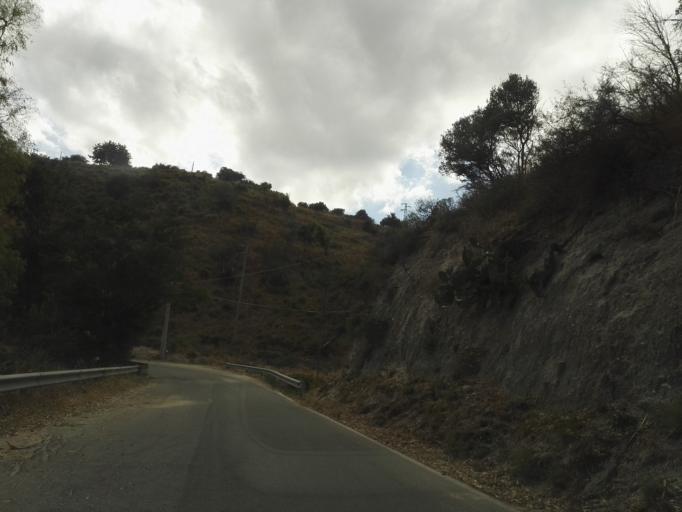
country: IT
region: Calabria
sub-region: Provincia di Reggio Calabria
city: Riace
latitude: 38.4223
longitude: 16.4819
